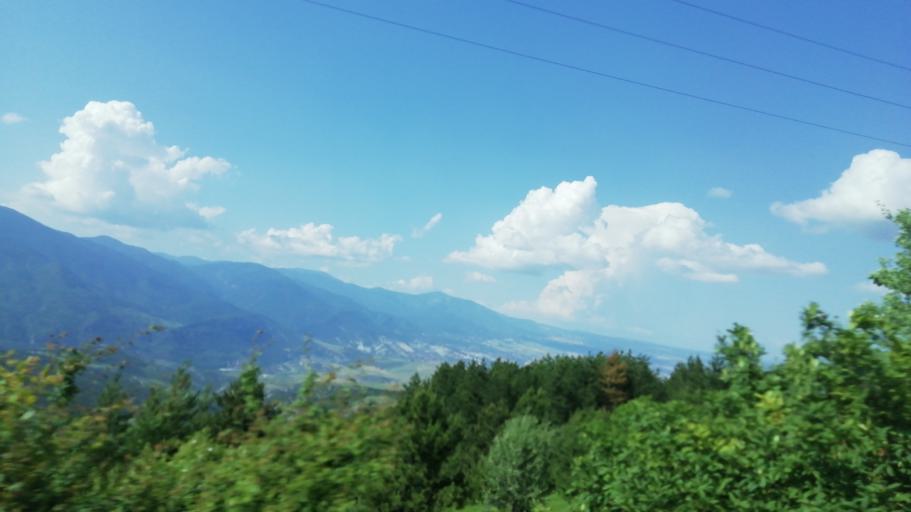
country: TR
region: Karabuk
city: Karabuk
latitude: 41.1247
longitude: 32.5829
